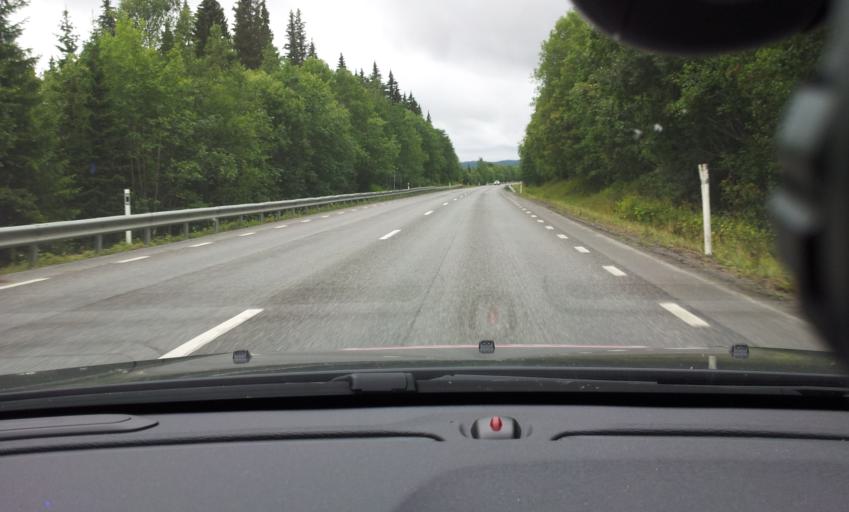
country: SE
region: Jaemtland
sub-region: Are Kommun
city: Are
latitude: 63.3970
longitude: 12.9620
